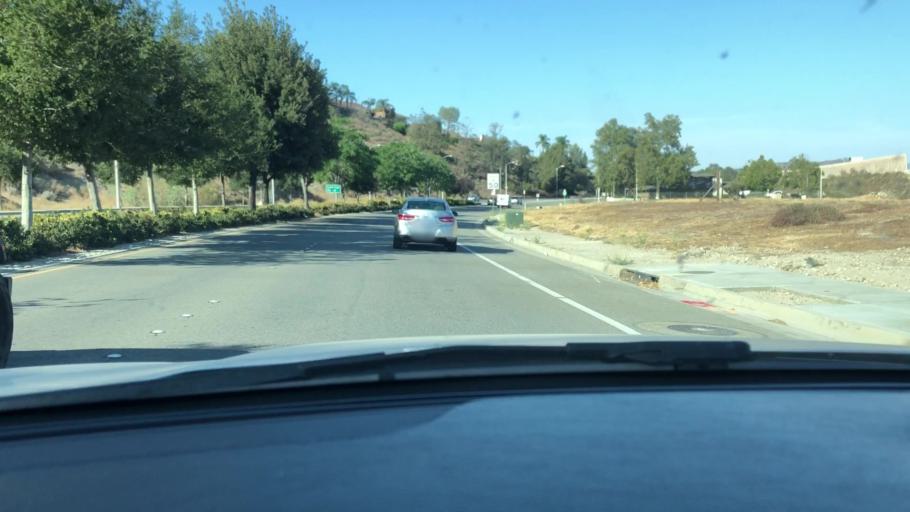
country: US
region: California
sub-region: Los Angeles County
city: Santa Clarita
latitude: 34.4189
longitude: -118.4393
